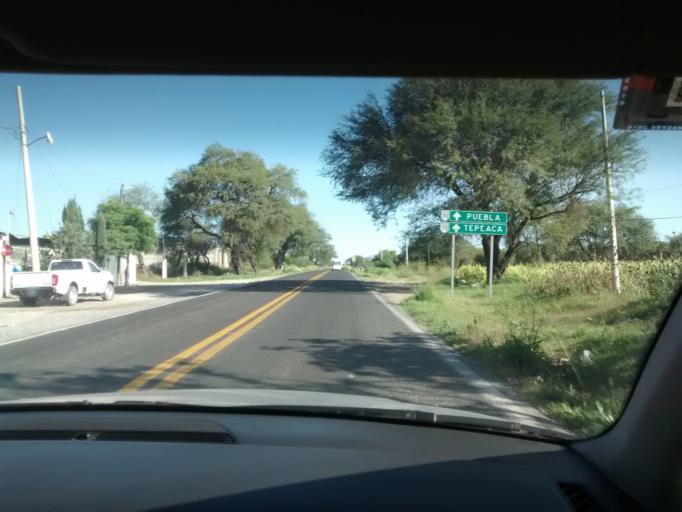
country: MX
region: Puebla
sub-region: Tepanco de Lopez
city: San Andres Cacaloapan
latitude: 18.5633
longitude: -97.5694
